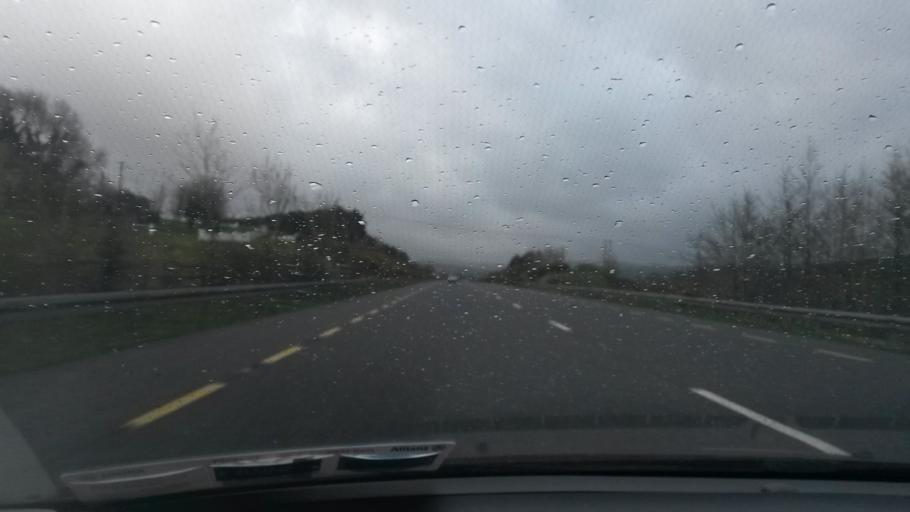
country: IE
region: Munster
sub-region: County Limerick
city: Abbeyfeale
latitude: 52.3237
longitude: -9.3593
